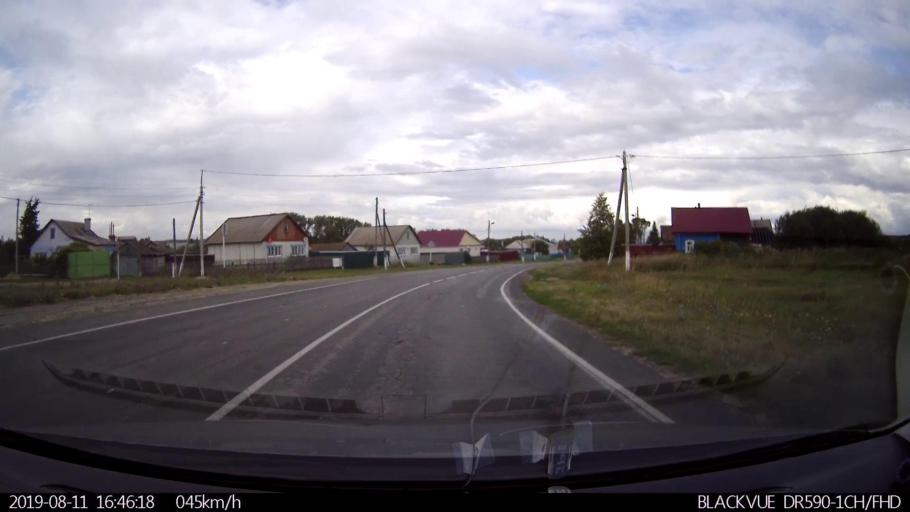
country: RU
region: Ulyanovsk
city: Mayna
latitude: 54.1972
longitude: 47.6875
